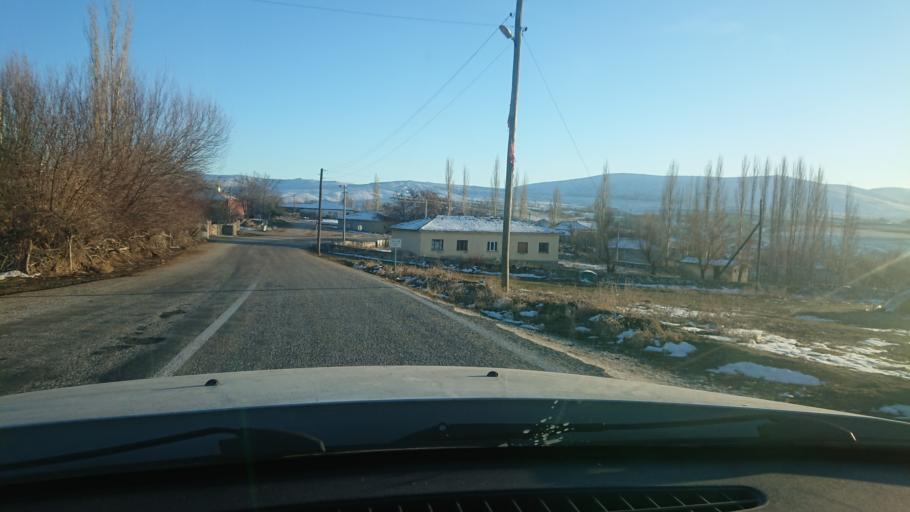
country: TR
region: Aksaray
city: Ortakoy
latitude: 38.7574
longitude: 33.9339
